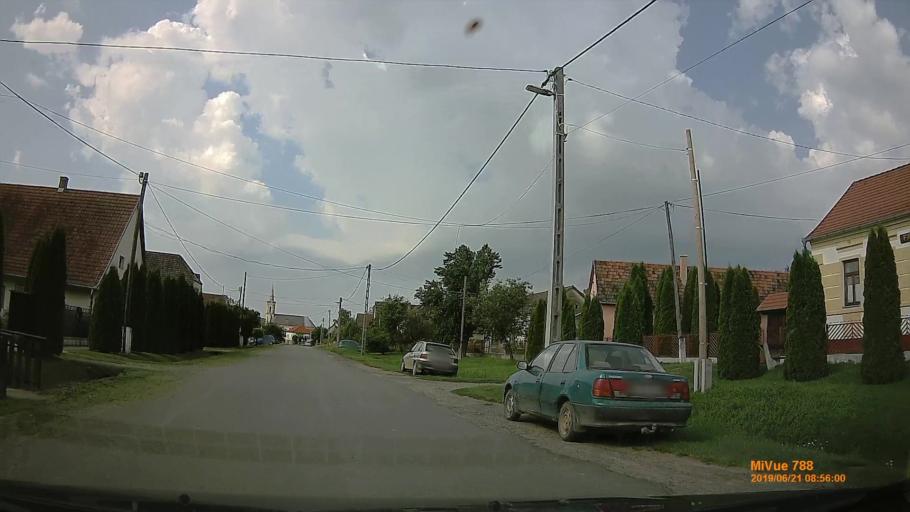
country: HU
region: Baranya
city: Buekkoesd
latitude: 46.1595
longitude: 17.8759
